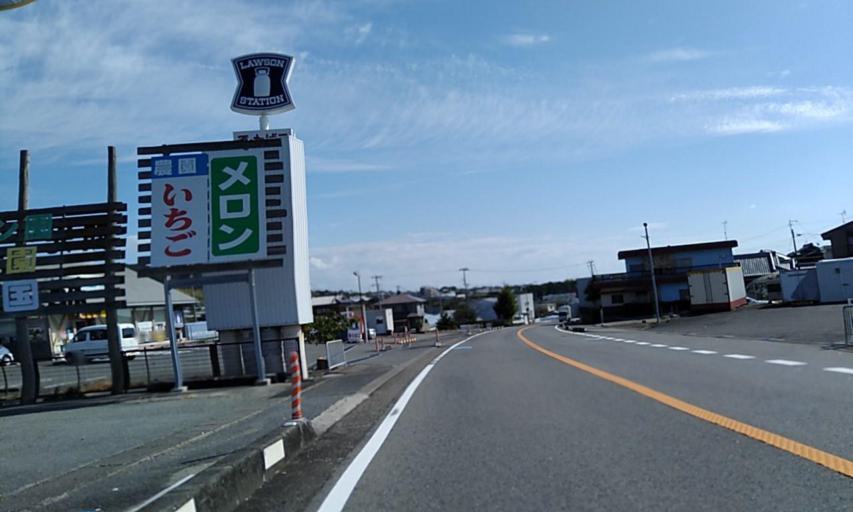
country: JP
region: Wakayama
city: Gobo
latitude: 33.8317
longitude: 135.1821
